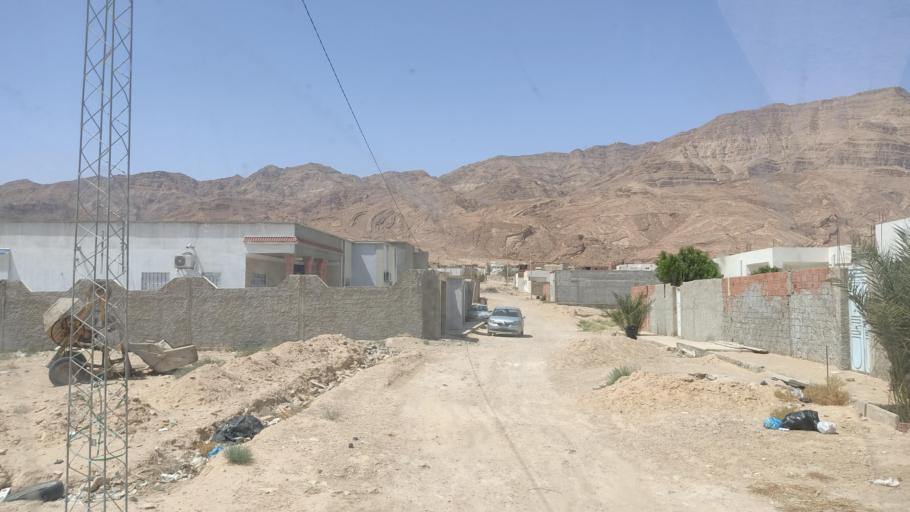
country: TN
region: Gafsa
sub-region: Gafsa Municipality
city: Gafsa
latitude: 34.3375
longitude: 8.9402
